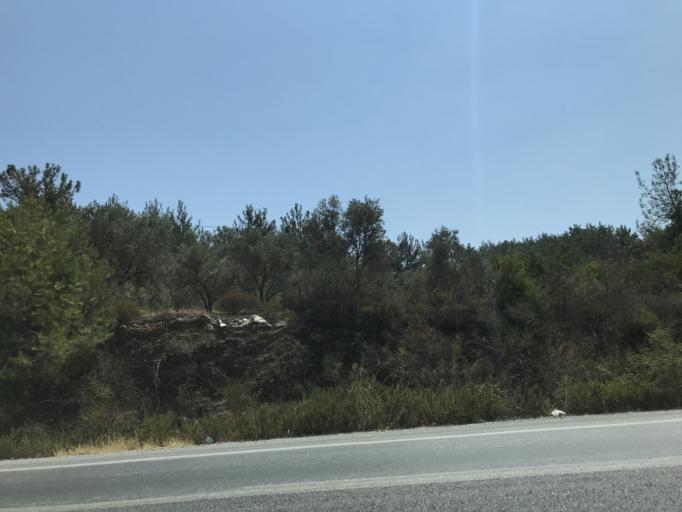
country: TR
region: Izmir
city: Selcuk
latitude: 37.8884
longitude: 27.3692
